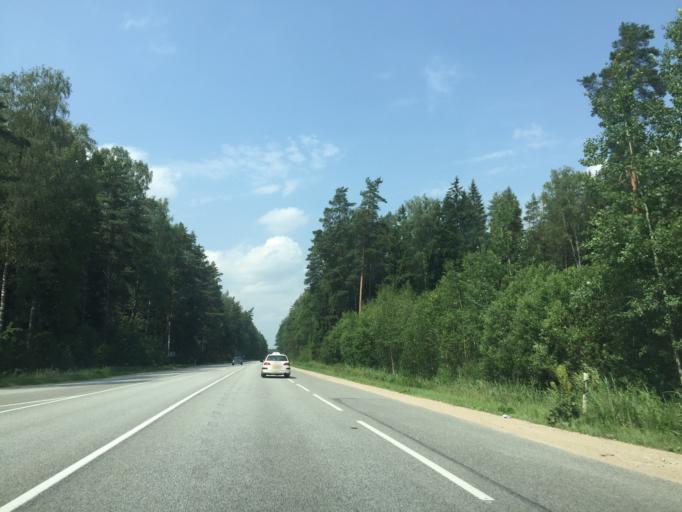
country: LV
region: Marupe
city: Marupe
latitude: 56.8279
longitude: 24.0561
